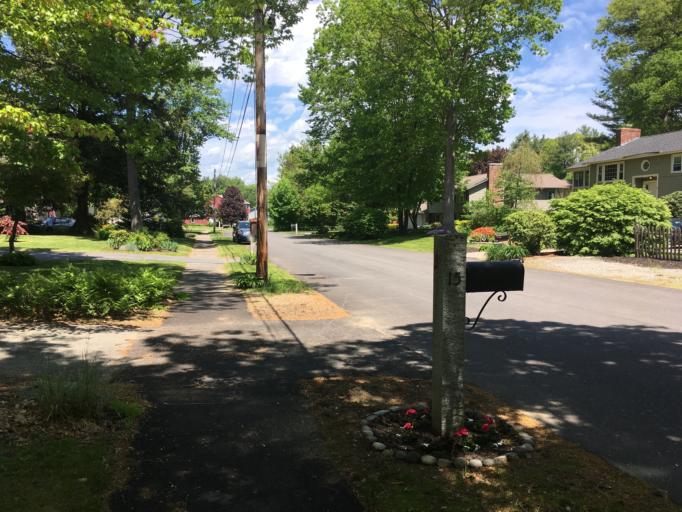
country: US
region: New Hampshire
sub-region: Rockingham County
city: Exeter
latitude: 42.9659
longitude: -70.9594
